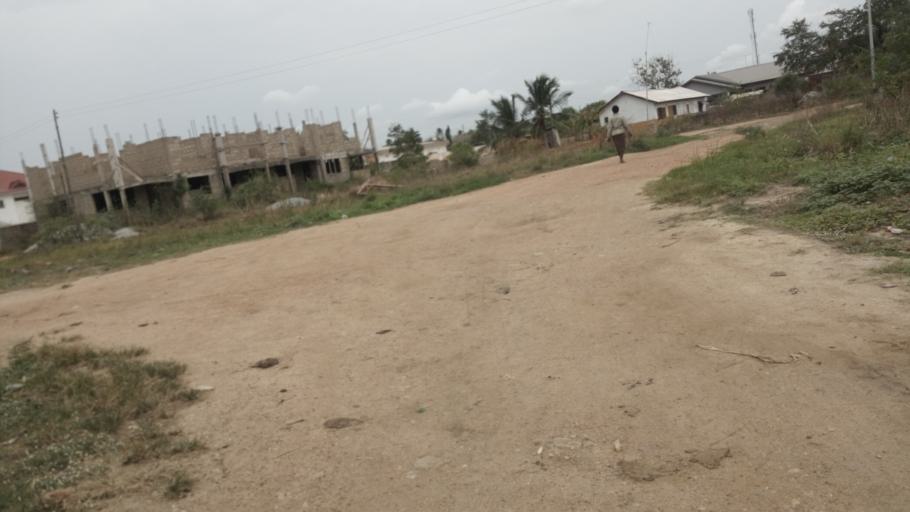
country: GH
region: Central
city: Winneba
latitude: 5.3665
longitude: -0.6404
